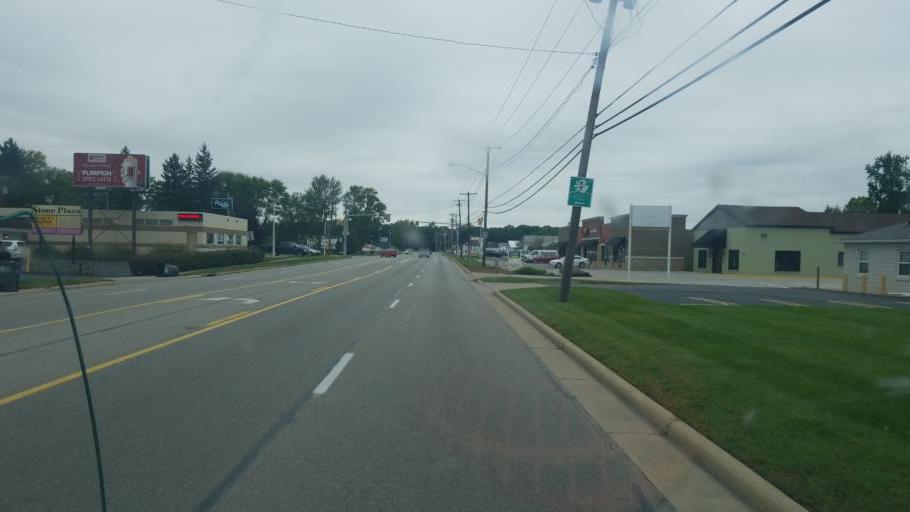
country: US
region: Ohio
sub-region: Lucas County
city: Ottawa Hills
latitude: 41.6681
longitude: -83.6679
